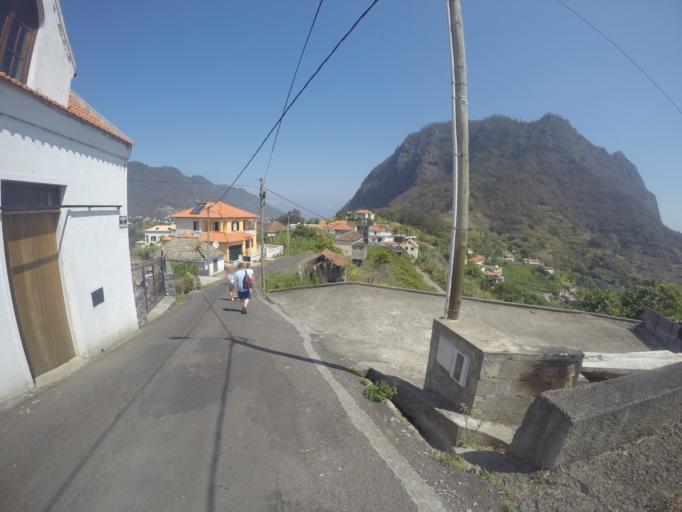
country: PT
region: Madeira
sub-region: Santana
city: Santana
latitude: 32.7582
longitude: -16.8424
